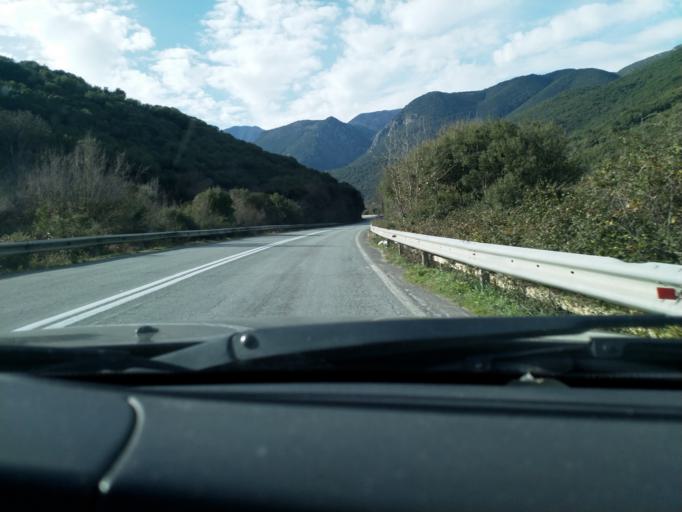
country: GR
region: Epirus
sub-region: Nomos Ioanninon
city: Agia Kyriaki
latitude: 39.4408
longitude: 20.8534
